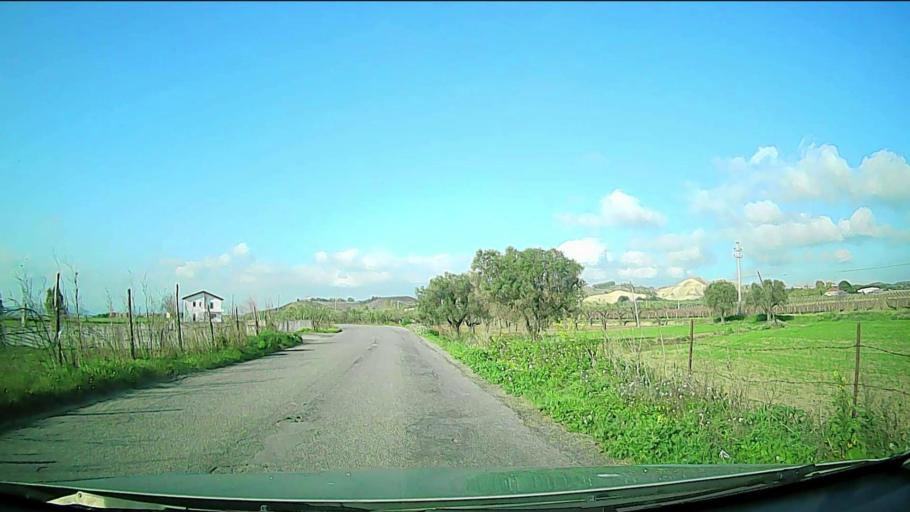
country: IT
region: Calabria
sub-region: Provincia di Crotone
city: Tronca
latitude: 39.2032
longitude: 17.0985
